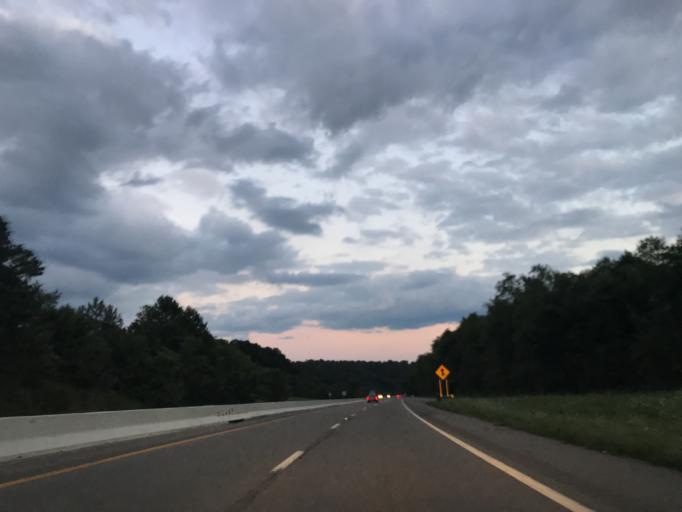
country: US
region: Ohio
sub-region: Columbiana County
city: Calcutta
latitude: 40.6636
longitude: -80.5907
